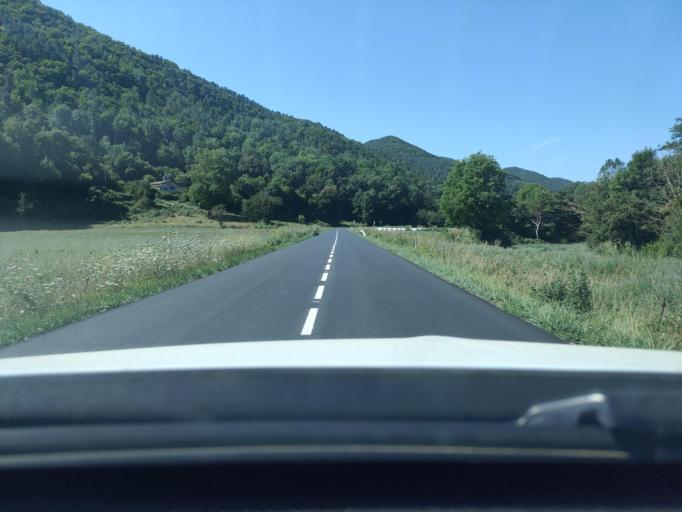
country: ES
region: Catalonia
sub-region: Provincia de Girona
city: Ripoll
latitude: 42.1763
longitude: 2.1768
